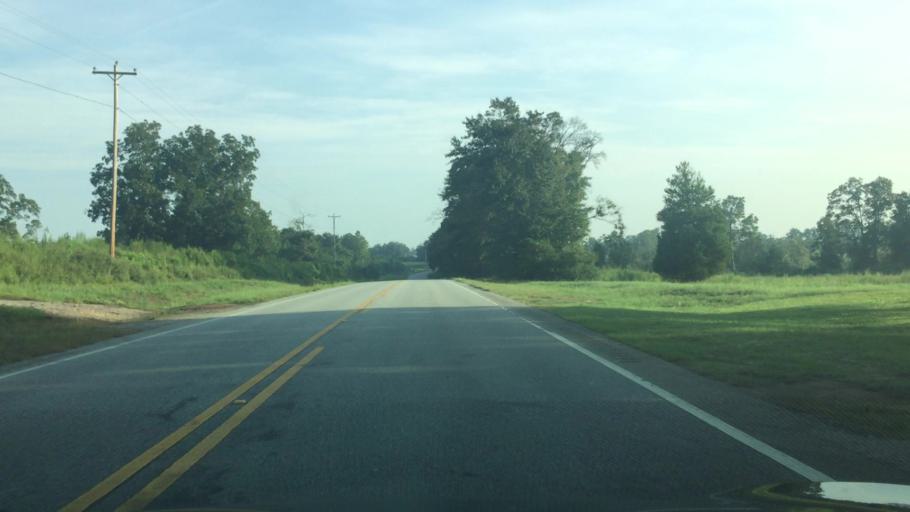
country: US
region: Alabama
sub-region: Covington County
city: Andalusia
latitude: 31.1629
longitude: -86.4593
